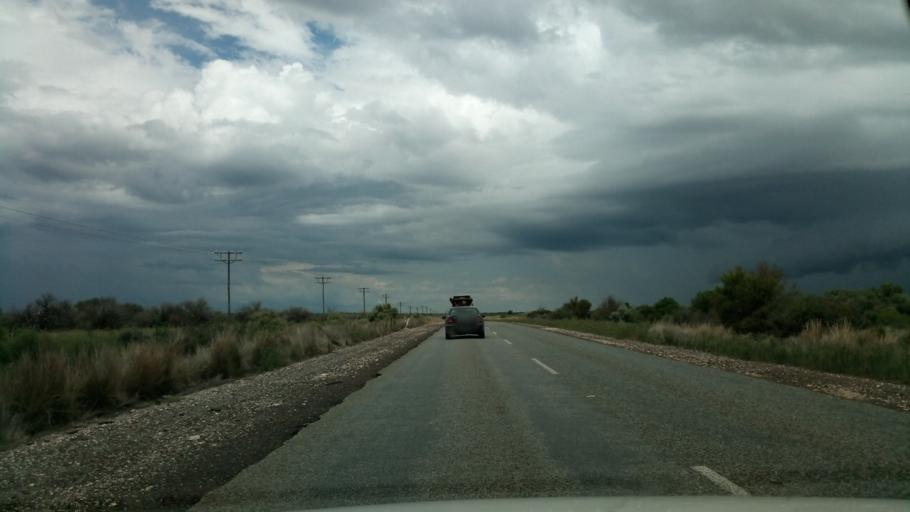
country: ZA
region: Northern Cape
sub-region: Frances Baard District Municipality
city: Barkly West
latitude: -28.2685
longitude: 24.0715
